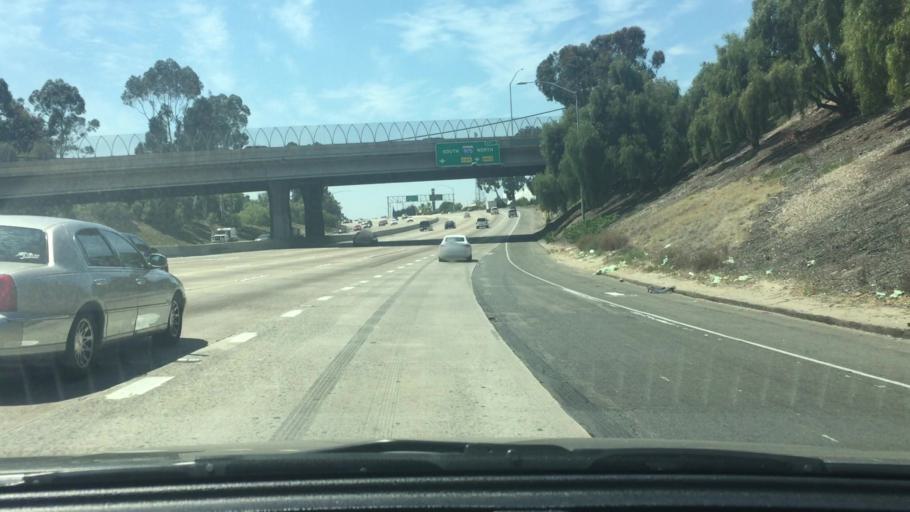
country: US
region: California
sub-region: San Diego County
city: National City
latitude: 32.7183
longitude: -117.0926
